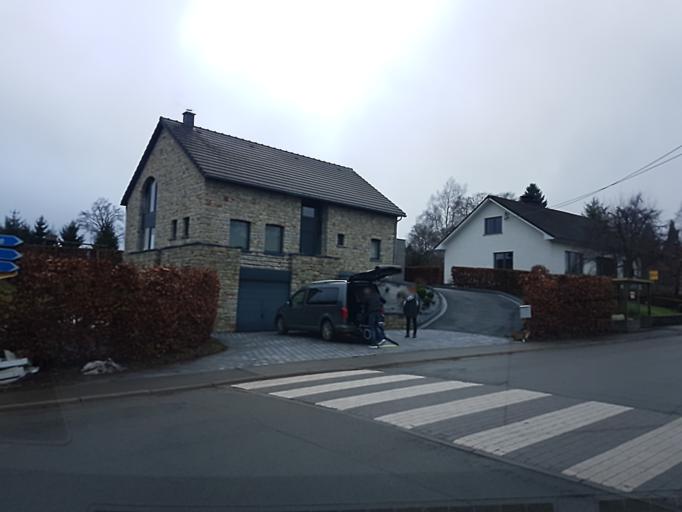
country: BE
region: Wallonia
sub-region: Province de Liege
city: Malmedy
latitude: 50.4630
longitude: 6.0672
